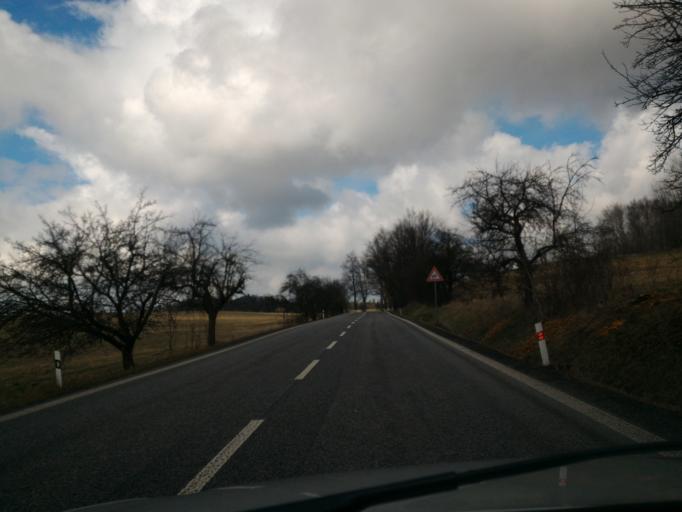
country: PL
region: Silesian Voivodeship
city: Zawidow
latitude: 50.9821
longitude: 15.0762
